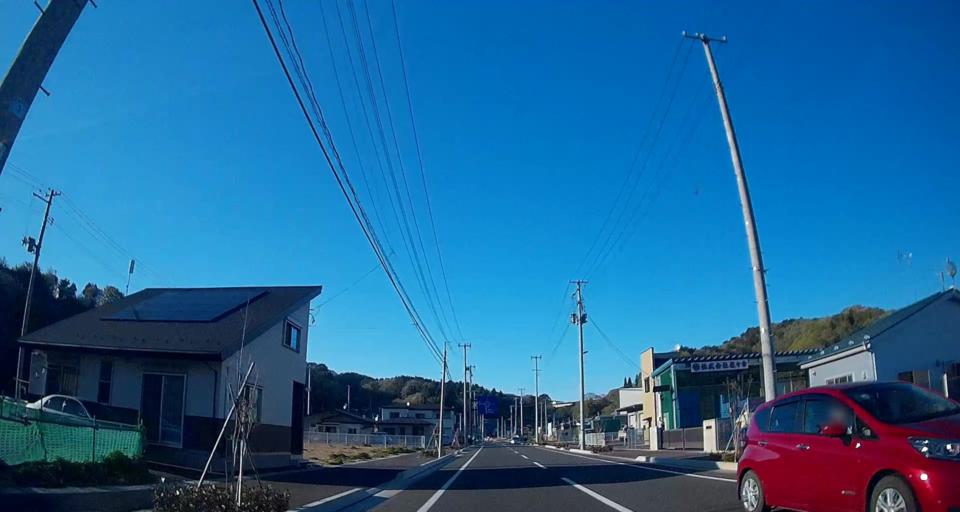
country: JP
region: Iwate
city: Miyako
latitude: 39.6460
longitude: 141.9678
